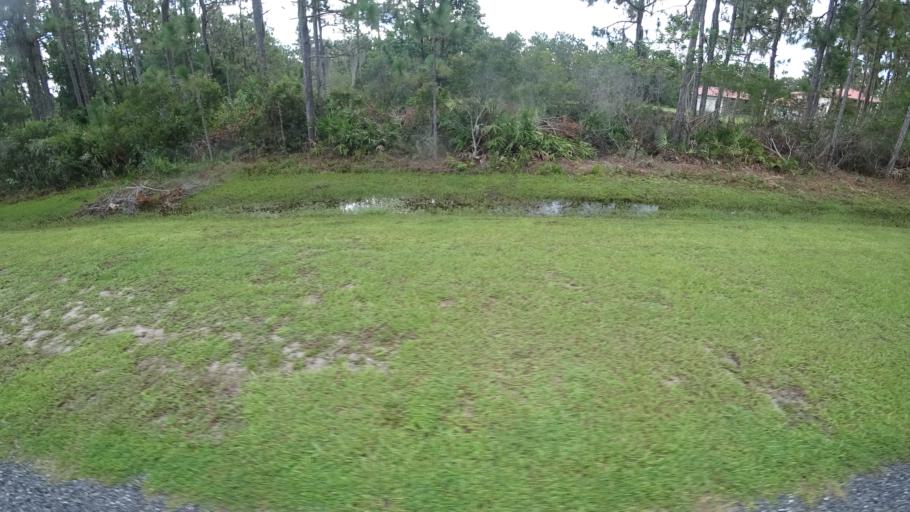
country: US
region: Florida
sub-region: Sarasota County
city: Lake Sarasota
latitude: 27.3968
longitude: -82.2793
